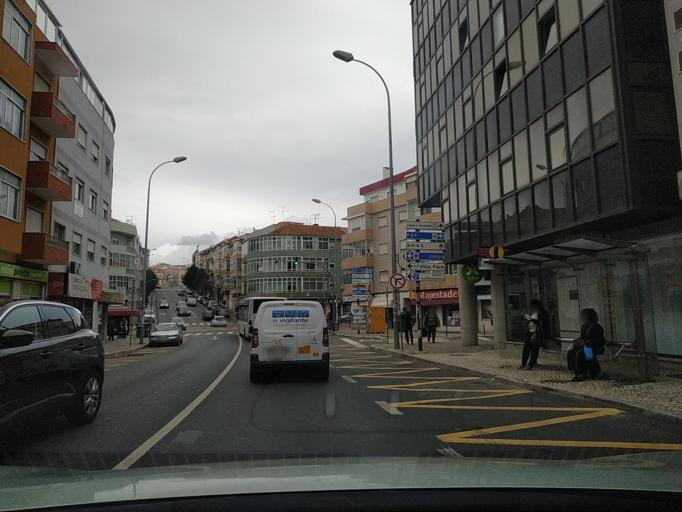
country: PT
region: Lisbon
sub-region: Amadora
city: Amadora
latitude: 38.7597
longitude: -9.2409
